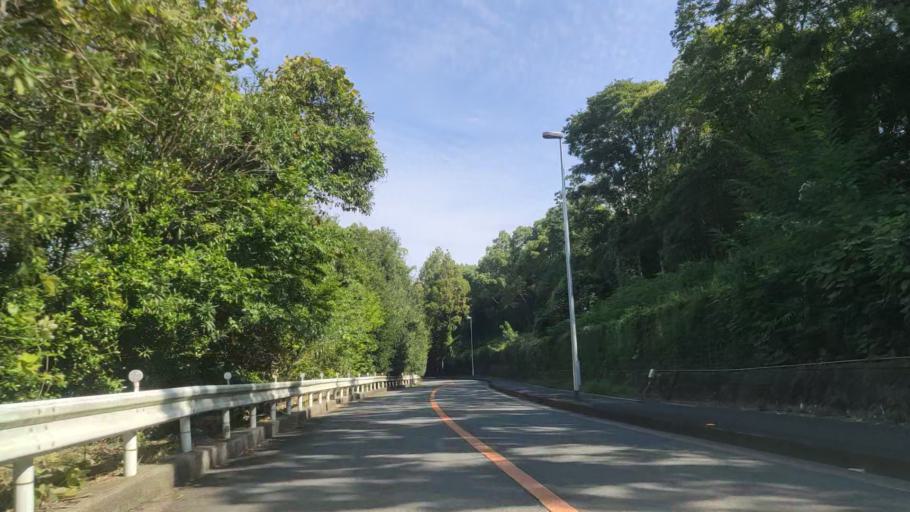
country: JP
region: Osaka
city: Ibaraki
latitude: 34.8147
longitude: 135.5192
